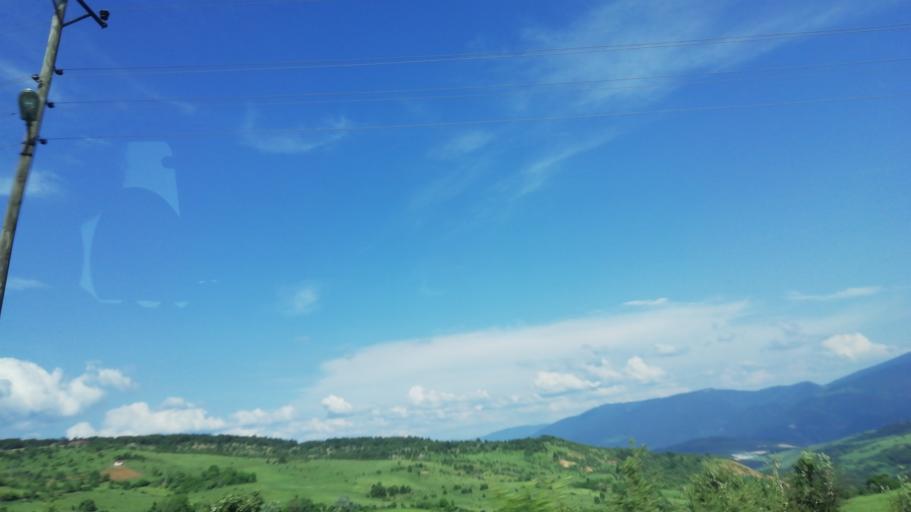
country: TR
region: Karabuk
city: Karabuk
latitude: 41.1029
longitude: 32.5951
